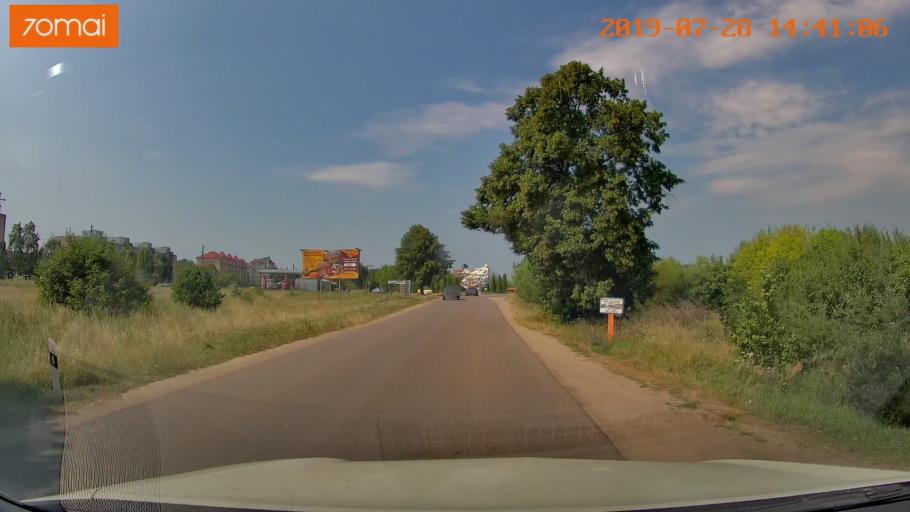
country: RU
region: Kaliningrad
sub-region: Gorod Kaliningrad
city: Yantarnyy
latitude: 54.8550
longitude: 19.9508
